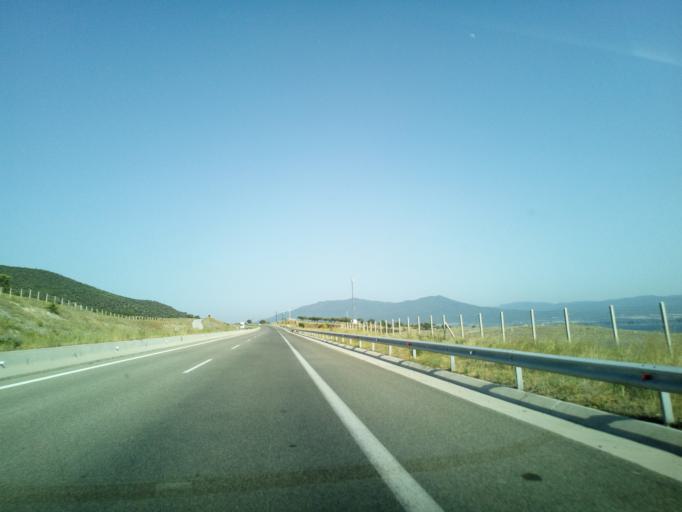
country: GR
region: Central Macedonia
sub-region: Nomos Thessalonikis
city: Nea Apollonia
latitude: 40.6850
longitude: 23.5461
